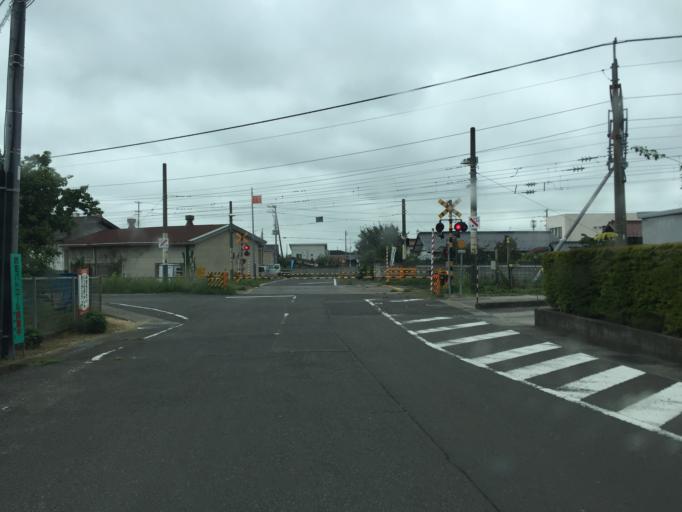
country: JP
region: Fukushima
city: Fukushima-shi
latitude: 37.7730
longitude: 140.3842
